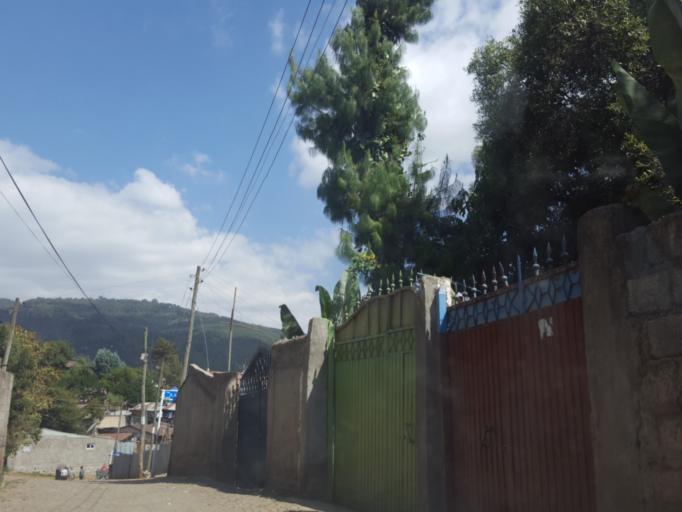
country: ET
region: Adis Abeba
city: Addis Ababa
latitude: 9.0622
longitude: 38.7643
